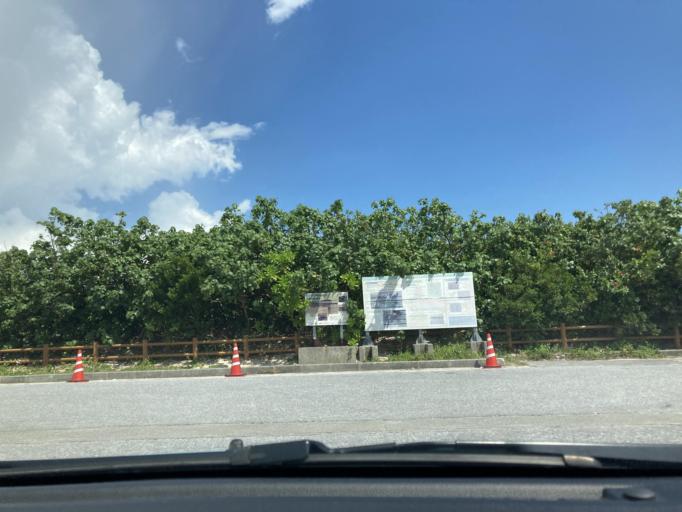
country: JP
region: Okinawa
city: Ginowan
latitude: 26.1822
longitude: 127.7788
